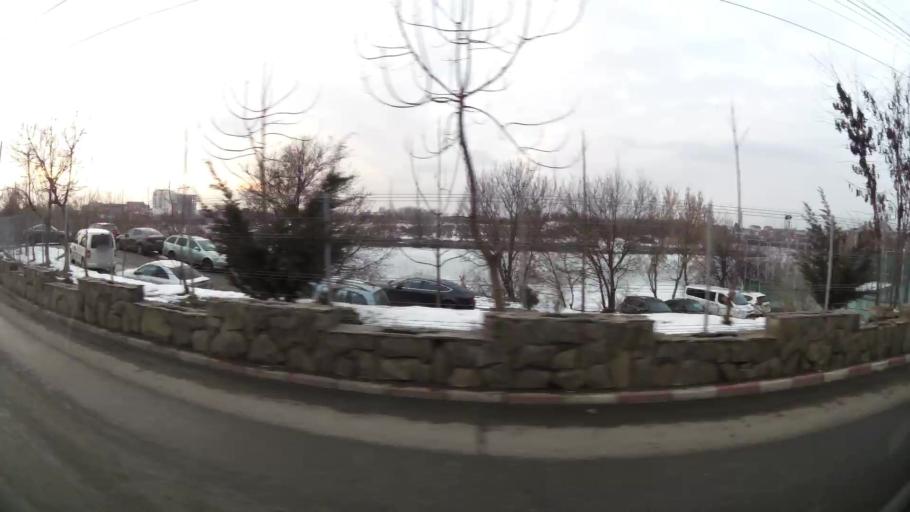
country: RO
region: Ilfov
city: Dobroesti
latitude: 44.4518
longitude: 26.1790
